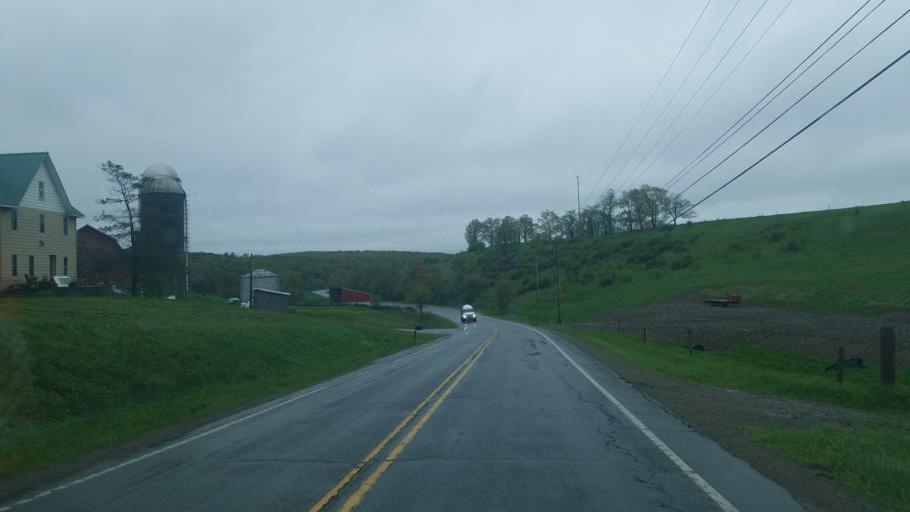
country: US
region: Pennsylvania
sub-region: Potter County
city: Coudersport
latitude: 41.8453
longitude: -77.8874
